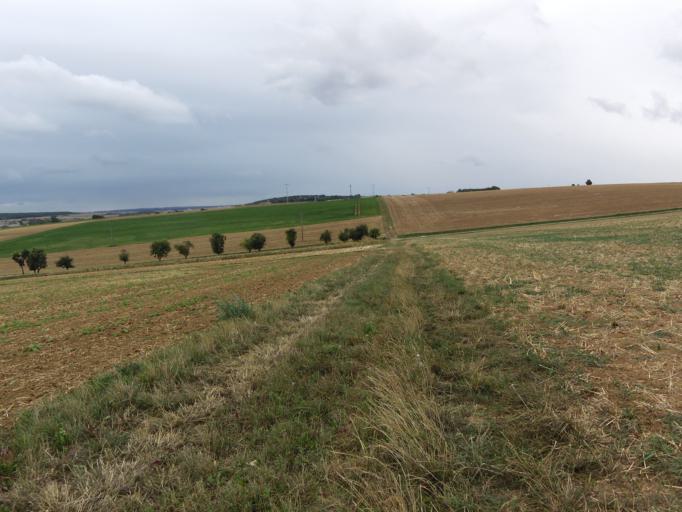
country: DE
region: Bavaria
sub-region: Regierungsbezirk Unterfranken
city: Rimpar
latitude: 49.8583
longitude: 9.9404
